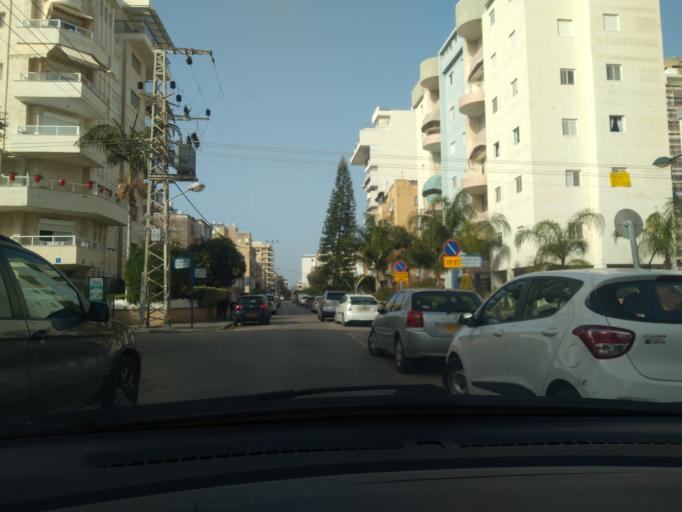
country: IL
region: Central District
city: Netanya
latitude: 32.3330
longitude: 34.8580
